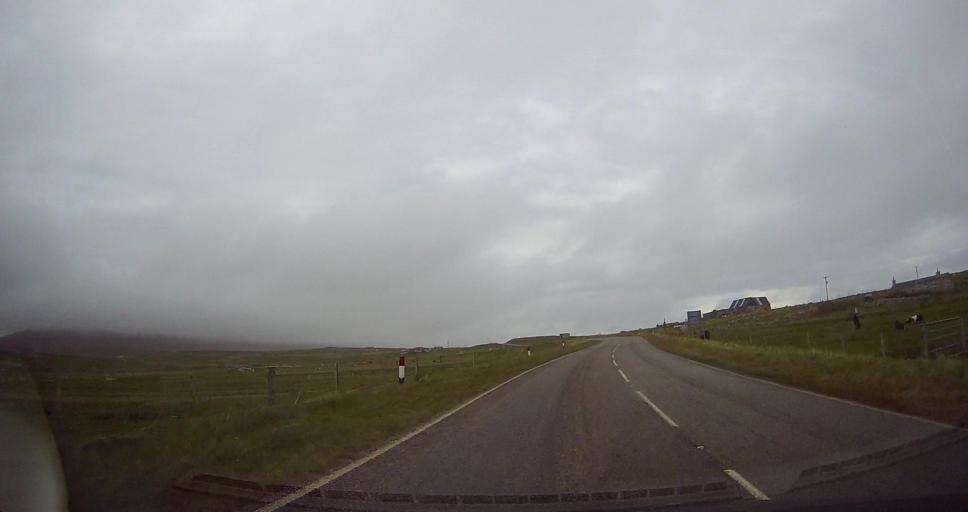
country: GB
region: Scotland
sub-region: Shetland Islands
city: Sandwick
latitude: 59.9294
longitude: -1.2970
